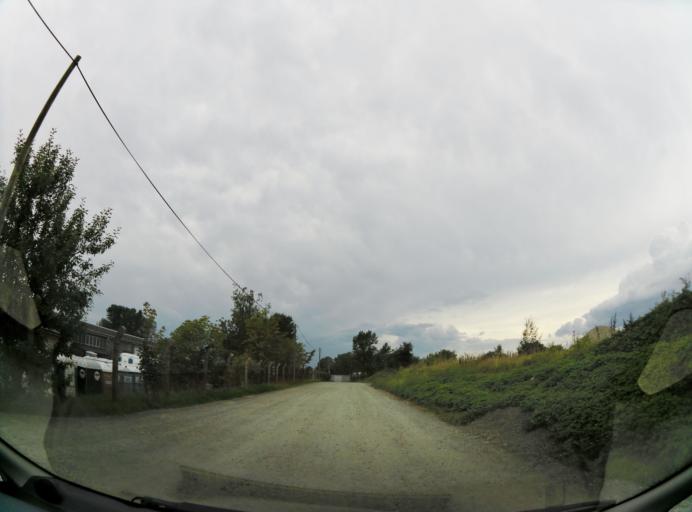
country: DE
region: Thuringia
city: Schleiz
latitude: 50.5638
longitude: 11.8307
